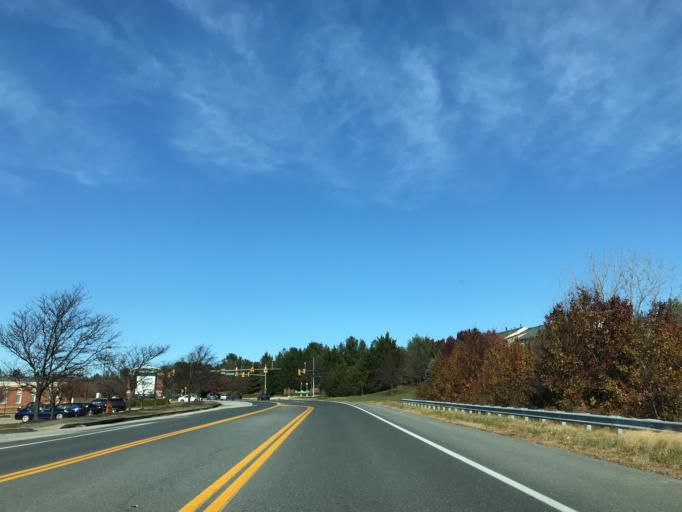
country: US
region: Maryland
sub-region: Howard County
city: Ilchester
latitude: 39.2096
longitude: -76.7770
